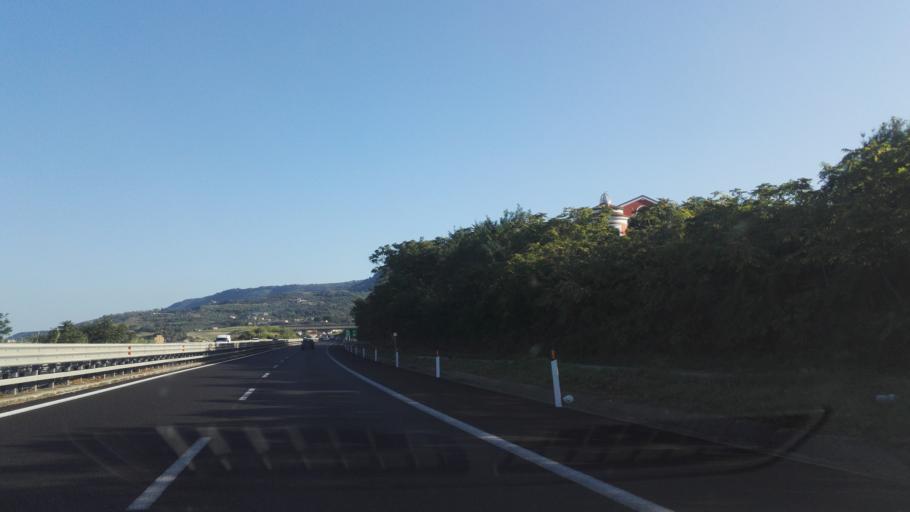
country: IT
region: Calabria
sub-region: Provincia di Catanzaro
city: Falerna Scalo
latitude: 38.9592
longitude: 16.1556
